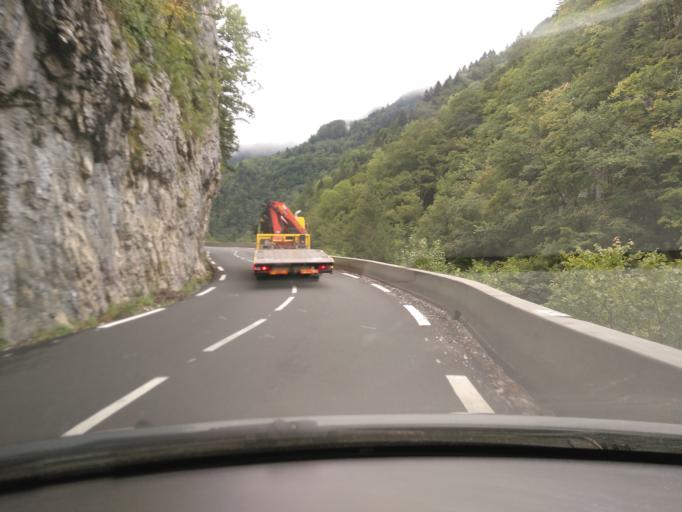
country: FR
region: Rhone-Alpes
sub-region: Departement de la Haute-Savoie
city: Bonneville
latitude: 46.0450
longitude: 6.3783
